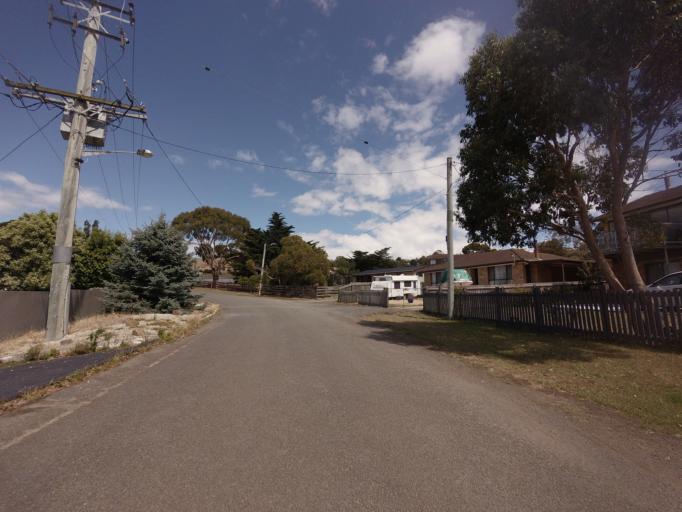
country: AU
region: Tasmania
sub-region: Clarence
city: Rokeby
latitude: -42.9106
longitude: 147.4321
